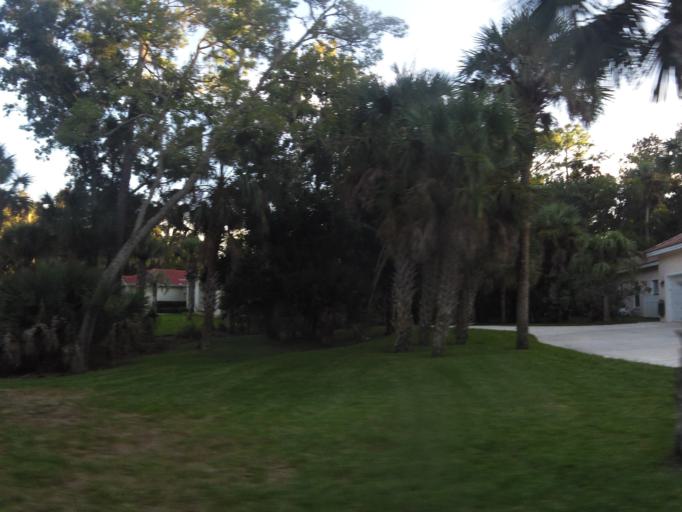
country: US
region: Florida
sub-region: Flagler County
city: Palm Coast
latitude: 29.5668
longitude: -81.1941
